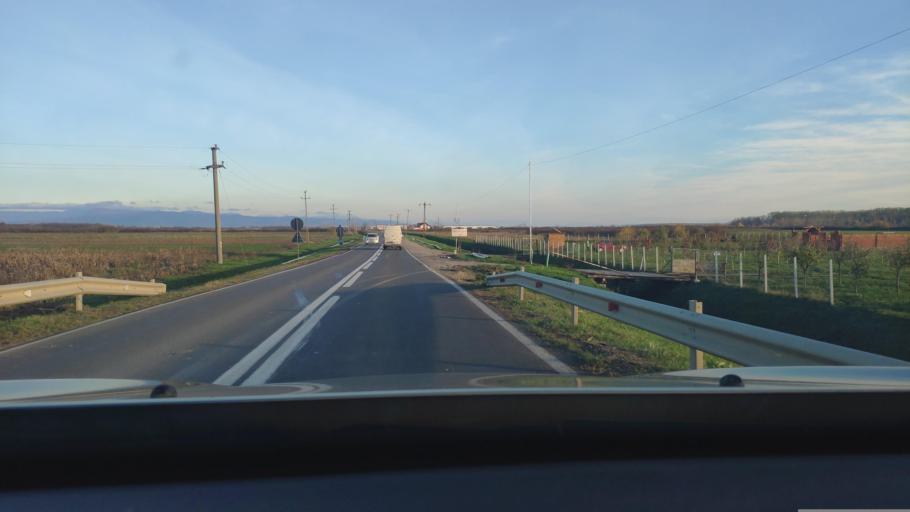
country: RO
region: Satu Mare
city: Culciu Mic
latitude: 47.7840
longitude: 23.0614
